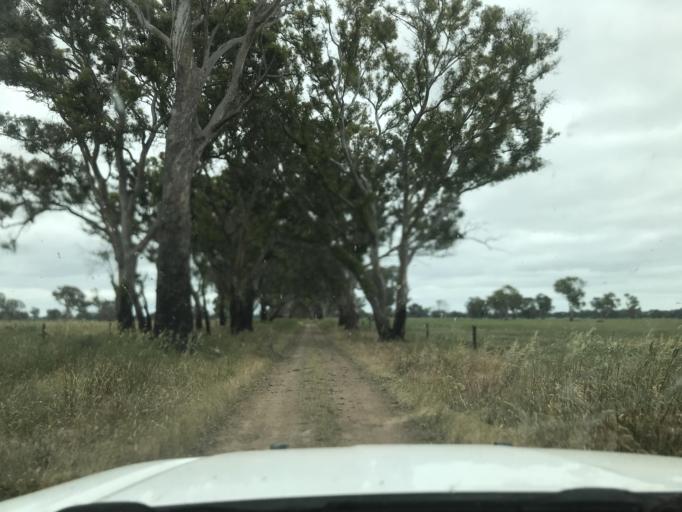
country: AU
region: South Australia
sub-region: Wattle Range
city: Penola
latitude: -37.1788
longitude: 141.0587
